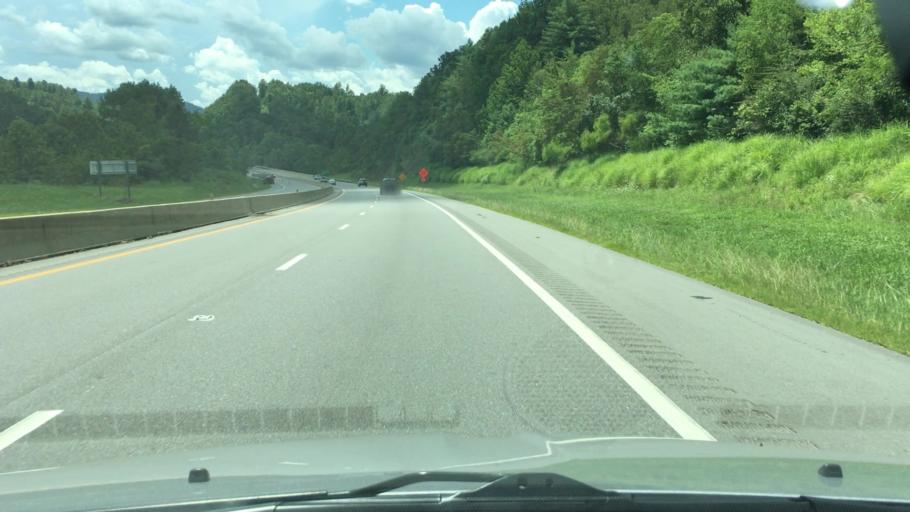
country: US
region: North Carolina
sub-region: Madison County
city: Mars Hill
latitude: 35.7956
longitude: -82.5392
